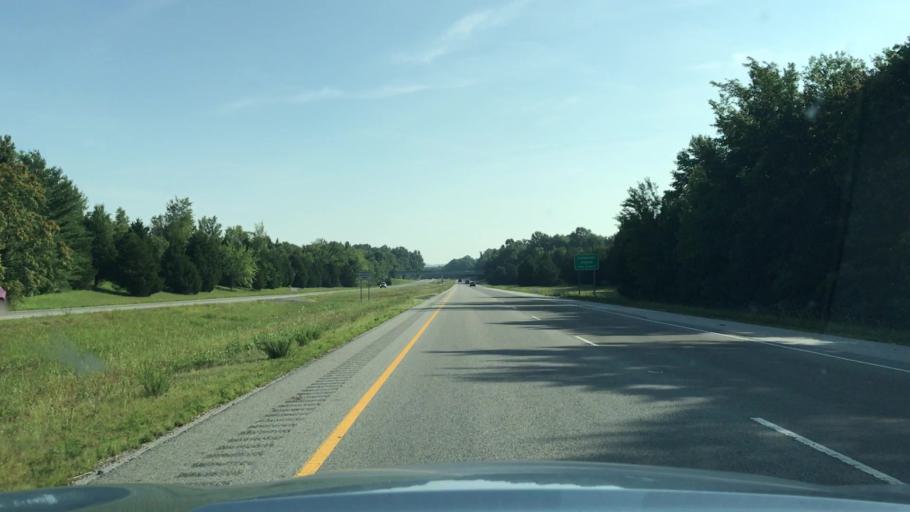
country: US
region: Tennessee
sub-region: Putnam County
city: Cookeville
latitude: 36.1627
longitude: -85.4668
